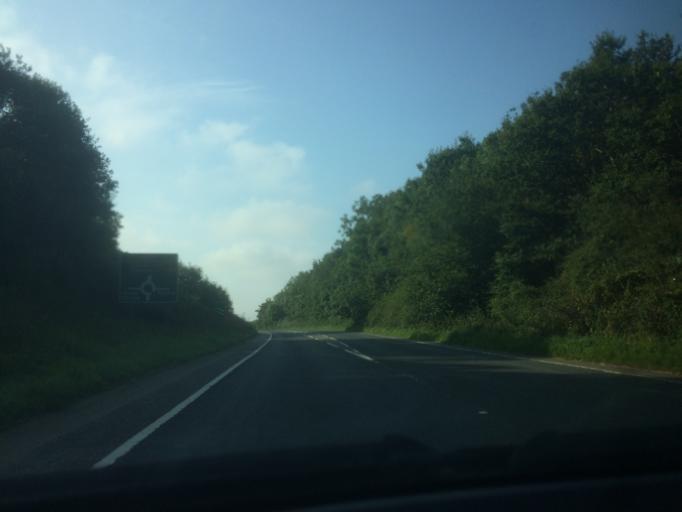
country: GB
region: England
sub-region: Cornwall
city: Saltash
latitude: 50.4388
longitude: -4.2570
